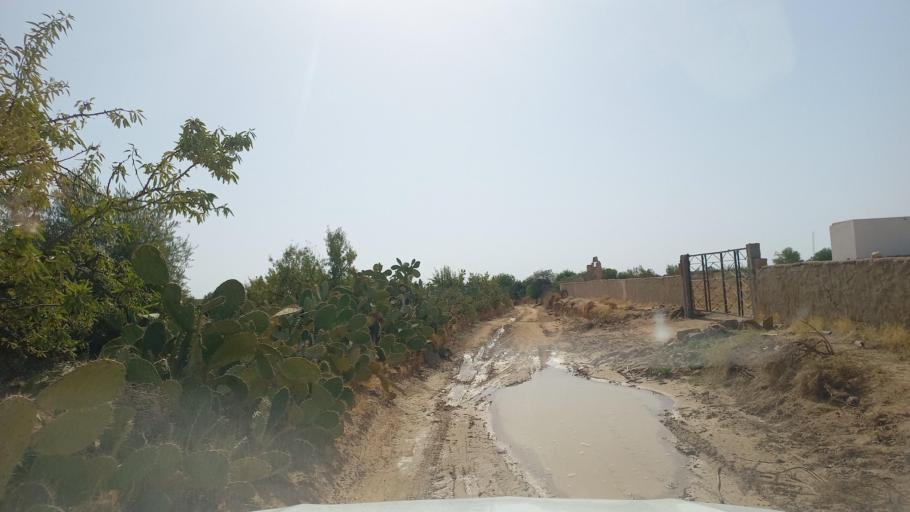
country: TN
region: Al Qasrayn
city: Kasserine
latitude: 35.2438
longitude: 9.0456
